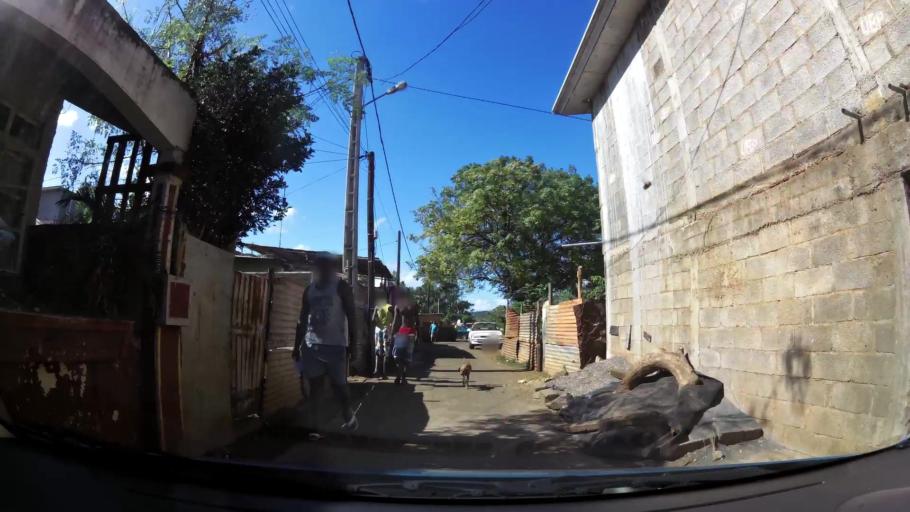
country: MU
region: Black River
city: Cascavelle
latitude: -20.2498
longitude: 57.4210
